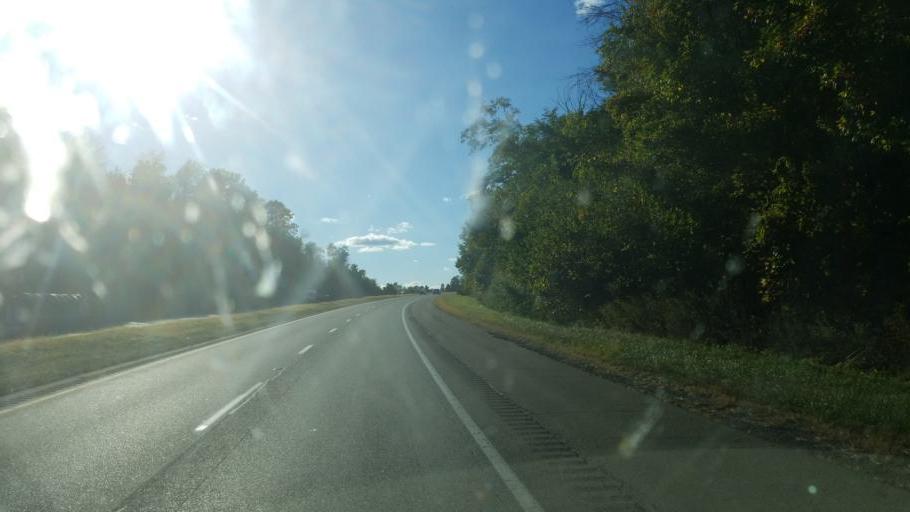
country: US
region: Ohio
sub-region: Belmont County
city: Barnesville
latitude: 40.0590
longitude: -81.1969
